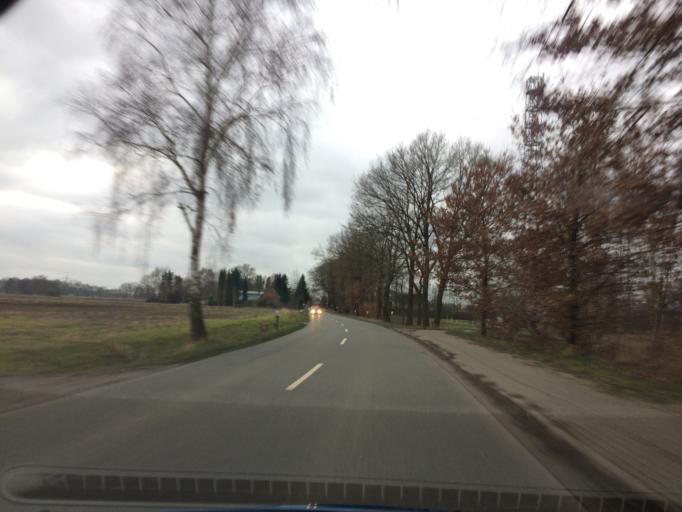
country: DE
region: Lower Saxony
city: Mechtersen
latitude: 53.3050
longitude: 10.3180
